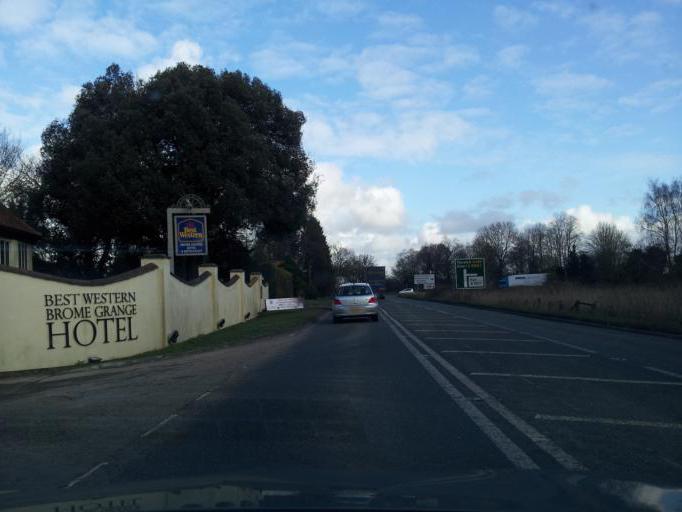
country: GB
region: England
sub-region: Norfolk
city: Diss
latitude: 52.3449
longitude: 1.1318
